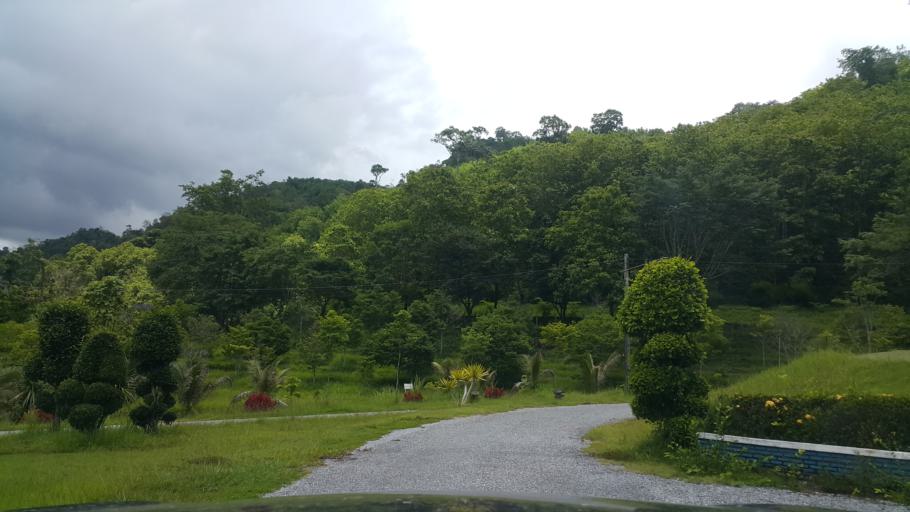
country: TH
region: Loei
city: Na Haeo
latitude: 17.6281
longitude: 100.8930
